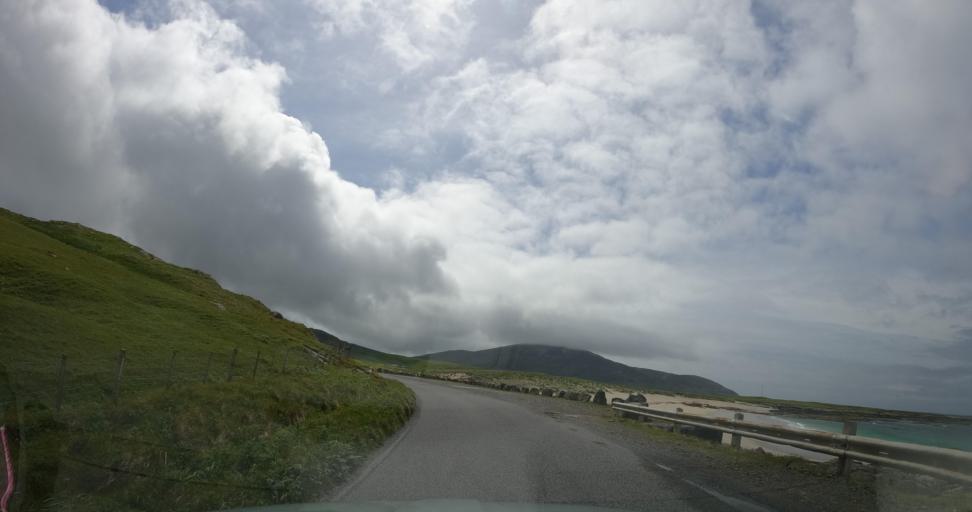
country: GB
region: Scotland
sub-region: Eilean Siar
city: Barra
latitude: 56.9901
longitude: -7.5095
